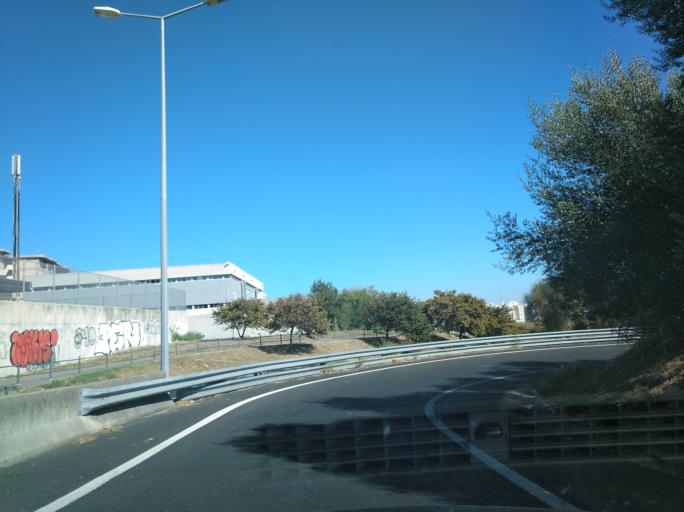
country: PT
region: Lisbon
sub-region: Loures
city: Moscavide
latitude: 38.7504
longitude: -9.1123
